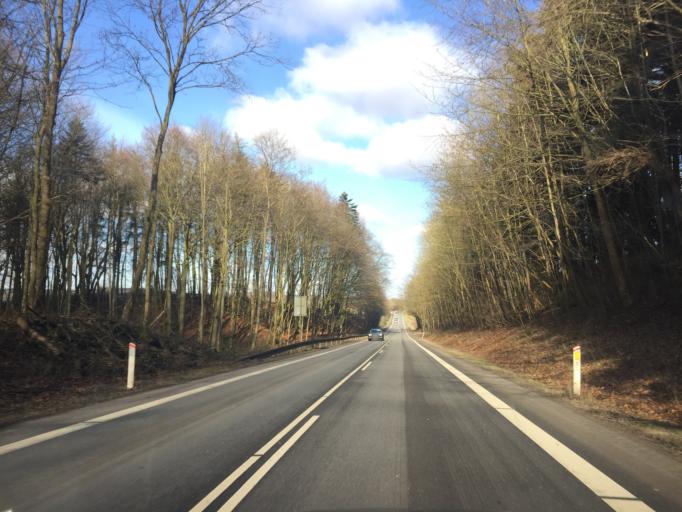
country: DK
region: South Denmark
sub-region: Assens Kommune
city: Vissenbjerg
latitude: 55.4343
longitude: 10.1840
